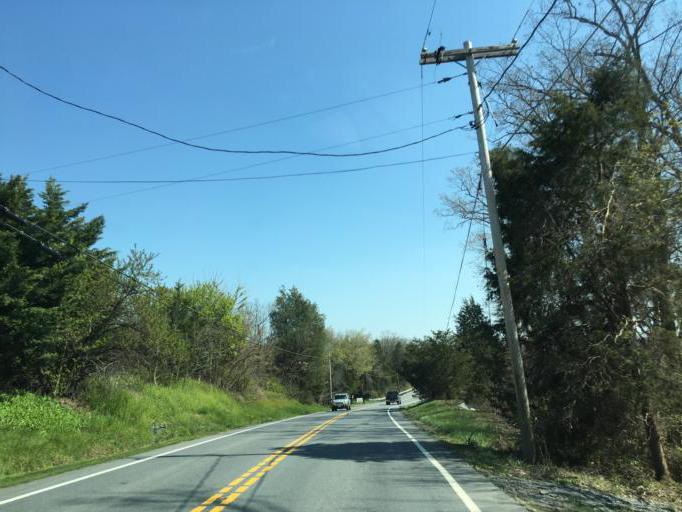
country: US
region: Maryland
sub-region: Frederick County
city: Woodsboro
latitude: 39.5148
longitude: -77.2846
